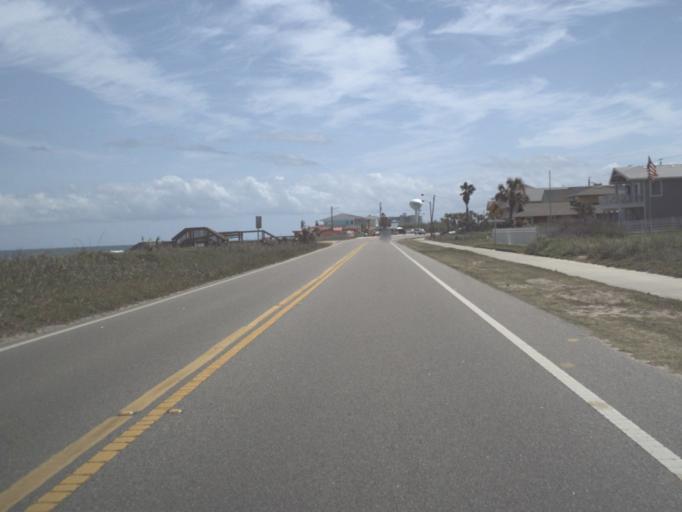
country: US
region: Florida
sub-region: Flagler County
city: Flagler Beach
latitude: 29.4449
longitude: -81.1107
